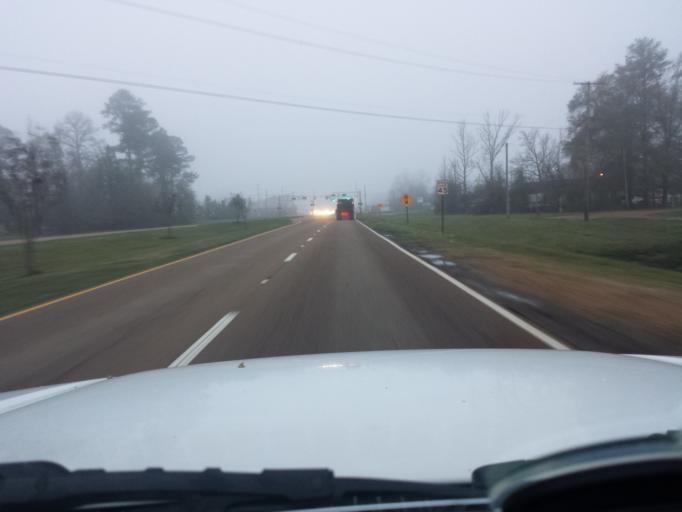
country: US
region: Mississippi
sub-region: Rankin County
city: Pearl
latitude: 32.2838
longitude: -90.1572
